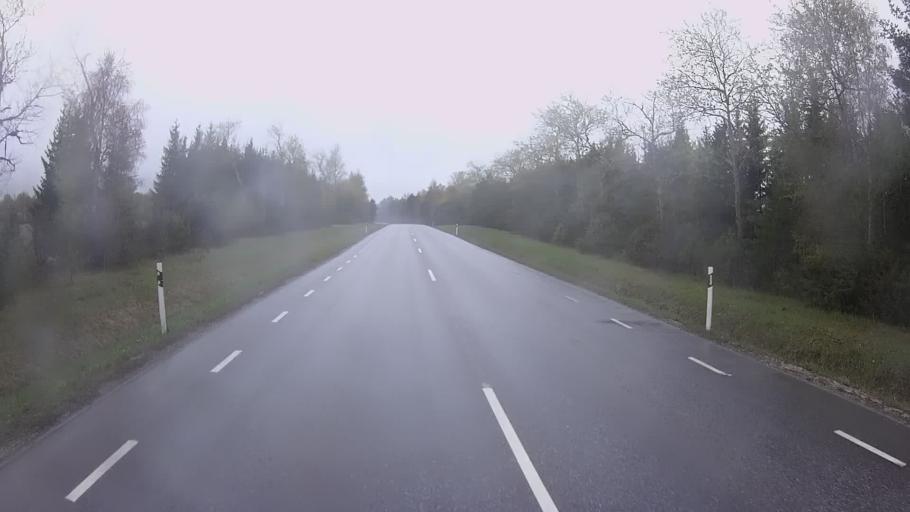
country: EE
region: Hiiumaa
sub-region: Kaerdla linn
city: Kardla
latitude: 58.9892
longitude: 22.5171
